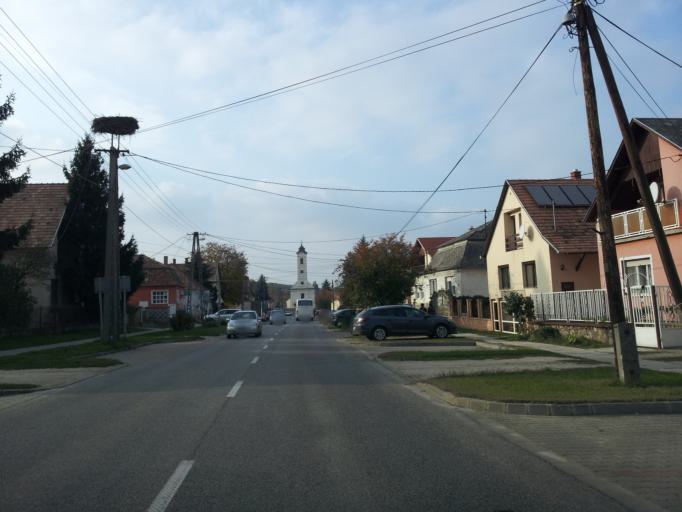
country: HU
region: Komarom-Esztergom
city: Bokod
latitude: 47.4924
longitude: 18.2460
